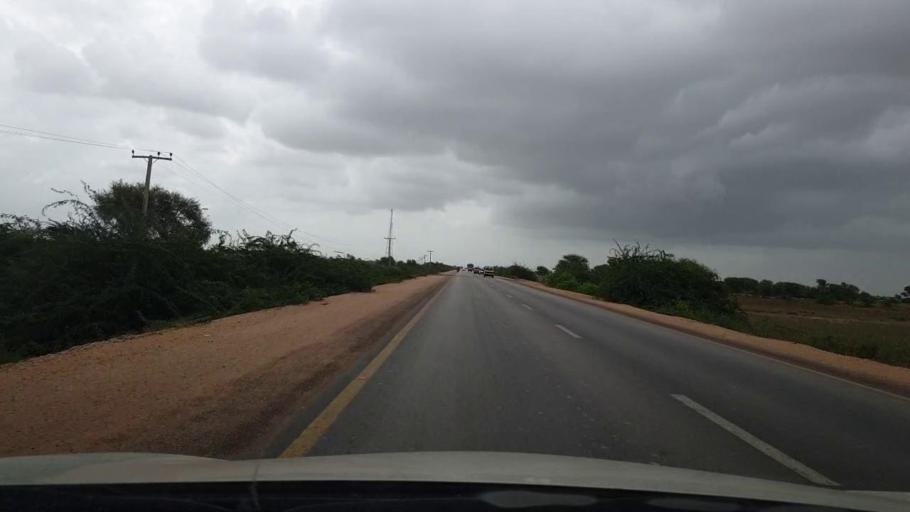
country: PK
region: Sindh
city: Mirpur Batoro
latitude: 24.6440
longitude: 68.4252
